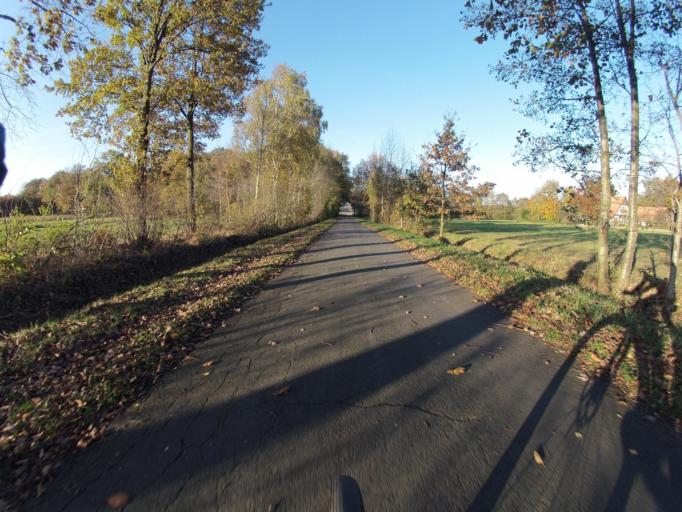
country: DE
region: North Rhine-Westphalia
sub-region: Regierungsbezirk Munster
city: Birgte
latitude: 52.2820
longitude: 7.6624
